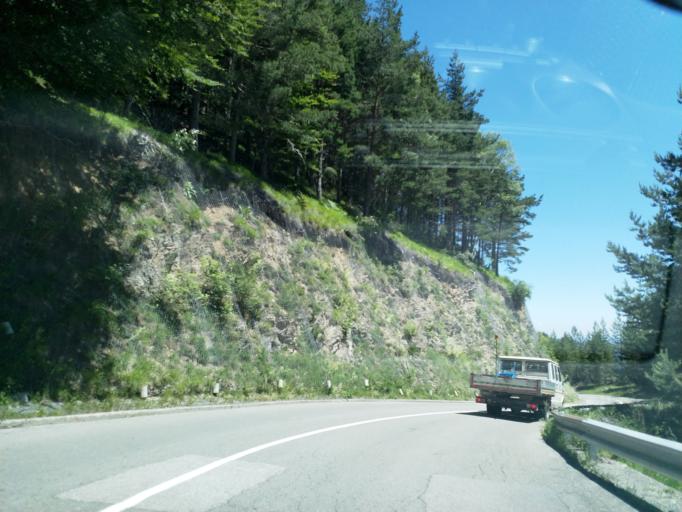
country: XK
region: Mitrovica
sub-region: Komuna e Leposaviqit
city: Leposaviq
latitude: 43.3114
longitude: 20.8646
